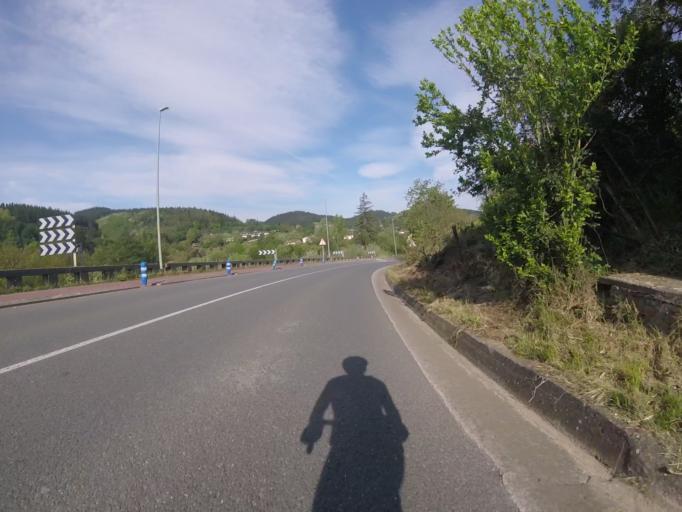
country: ES
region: Basque Country
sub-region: Provincia de Guipuzcoa
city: Ormaiztegui
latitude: 43.0417
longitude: -2.2506
